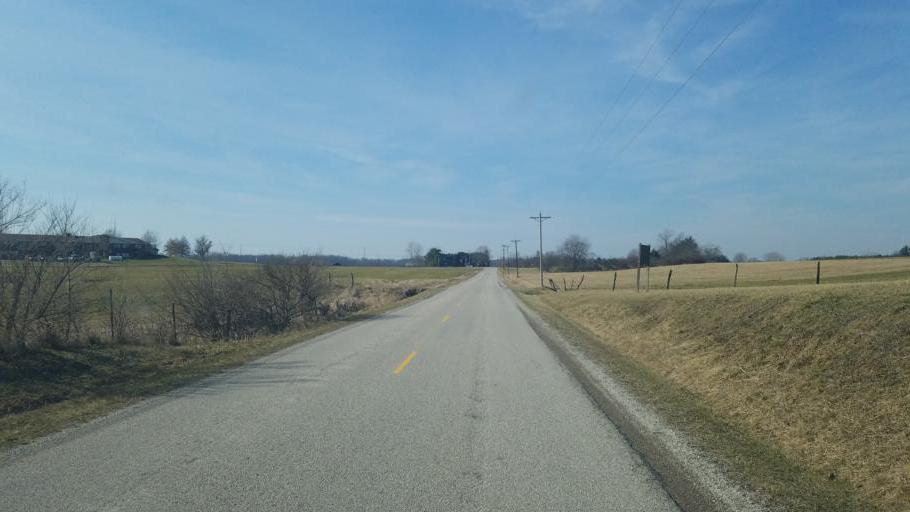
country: US
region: Ohio
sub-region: Ashland County
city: Ashland
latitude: 40.8057
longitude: -82.2659
